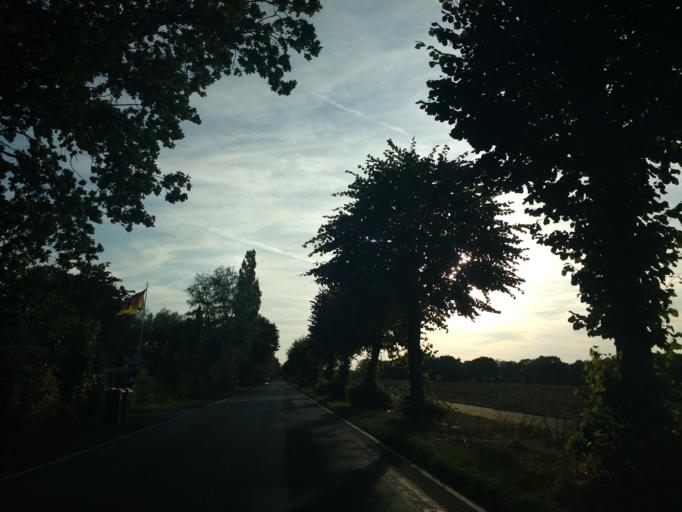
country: DE
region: North Rhine-Westphalia
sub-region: Regierungsbezirk Detmold
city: Hovelhof
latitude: 51.8679
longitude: 8.6781
